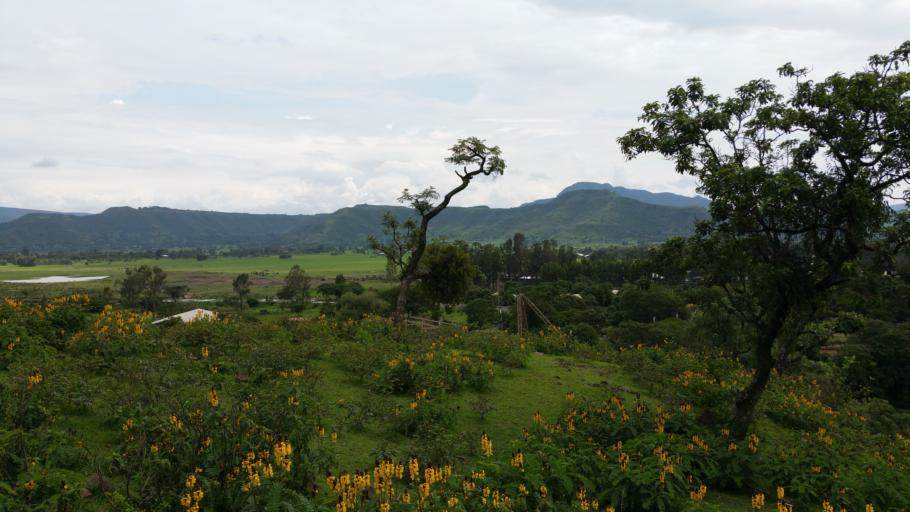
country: ET
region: Amhara
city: Bahir Dar
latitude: 11.4870
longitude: 37.5906
